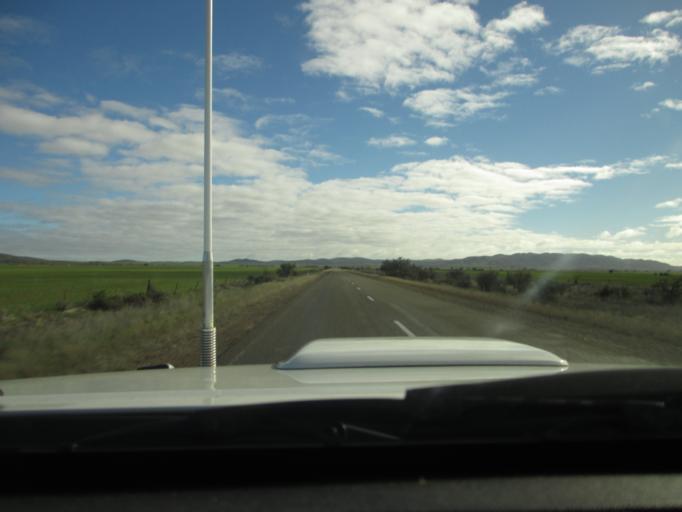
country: AU
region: South Australia
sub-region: Peterborough
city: Peterborough
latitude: -32.6602
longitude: 138.6050
